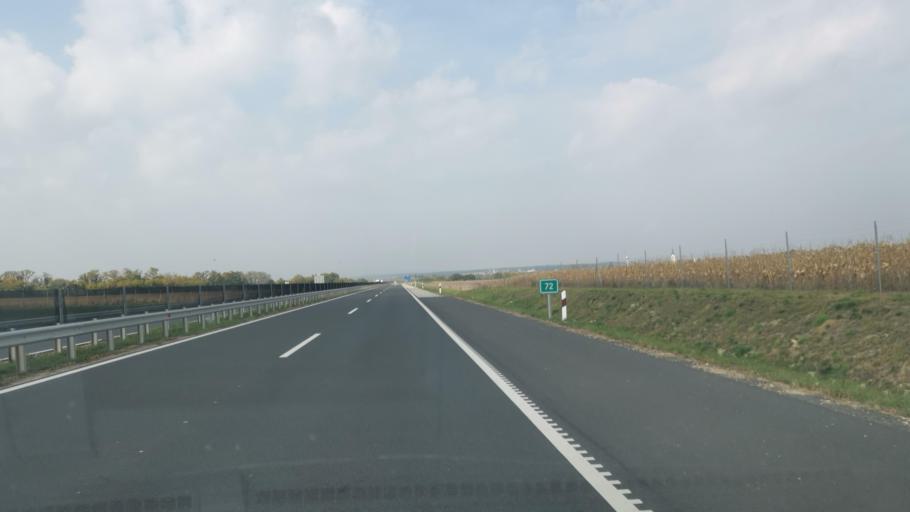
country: HU
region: Gyor-Moson-Sopron
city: Nagycenk
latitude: 47.5924
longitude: 16.7052
